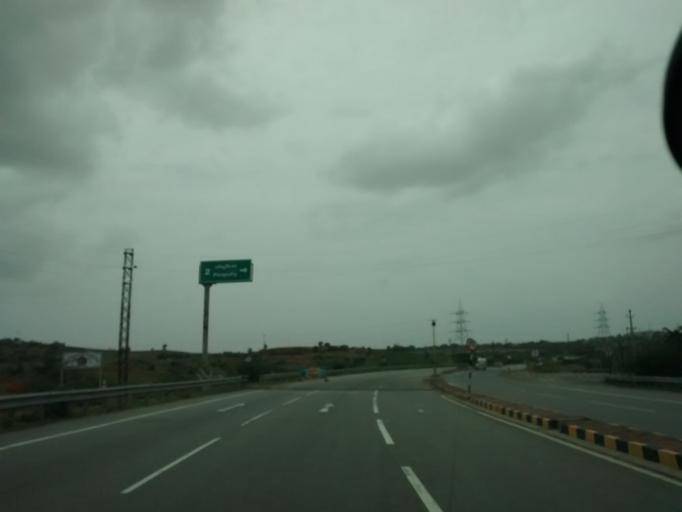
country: IN
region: Andhra Pradesh
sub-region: Kurnool
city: Ramapuram
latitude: 15.2192
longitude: 77.7226
